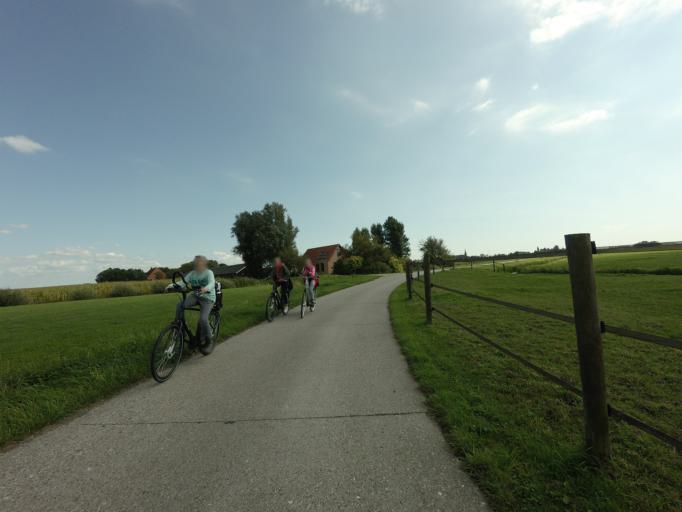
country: NL
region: Friesland
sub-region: Gemeente Littenseradiel
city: Makkum
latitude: 53.0852
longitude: 5.6319
